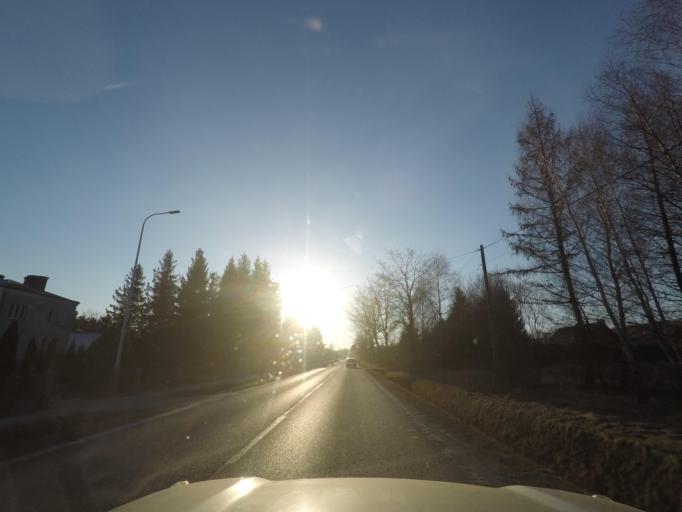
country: PL
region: Subcarpathian Voivodeship
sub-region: Powiat krosnienski
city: Dukla
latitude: 49.5582
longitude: 21.6641
